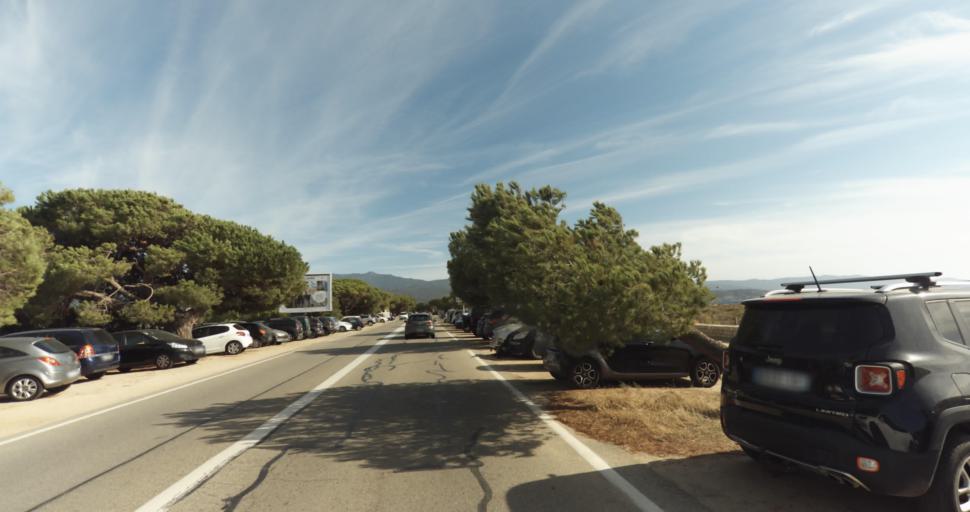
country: FR
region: Corsica
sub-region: Departement de la Corse-du-Sud
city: Ajaccio
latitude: 41.9220
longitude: 8.7862
